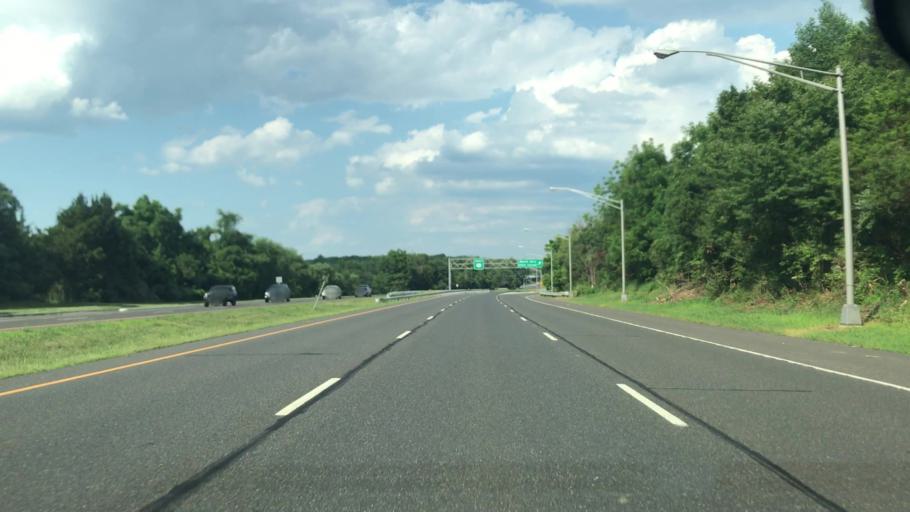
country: US
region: New Jersey
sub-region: Hunterdon County
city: Lambertville
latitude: 40.4002
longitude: -74.9178
